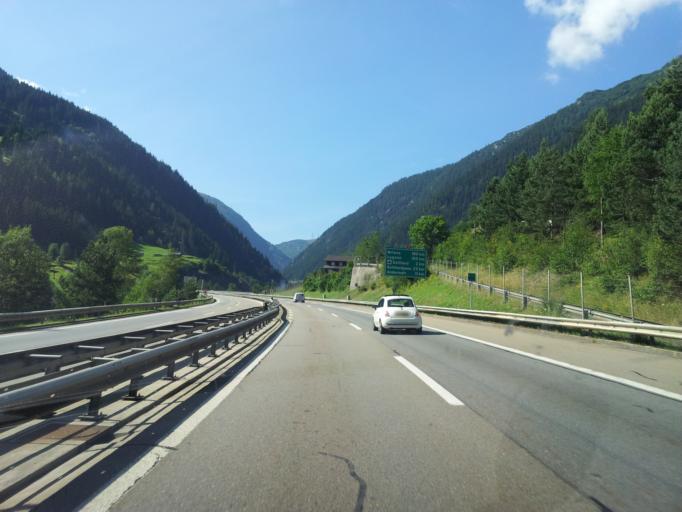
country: CH
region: Uri
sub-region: Uri
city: Andermatt
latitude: 46.6998
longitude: 8.5966
